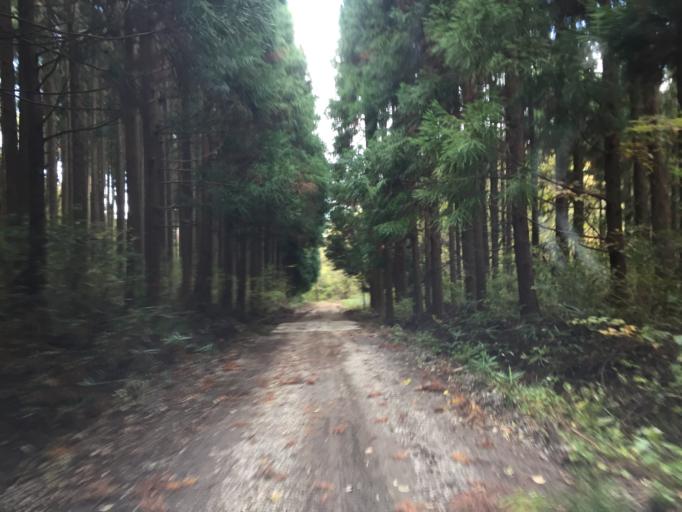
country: JP
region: Fukushima
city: Fukushima-shi
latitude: 37.6848
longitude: 140.3788
